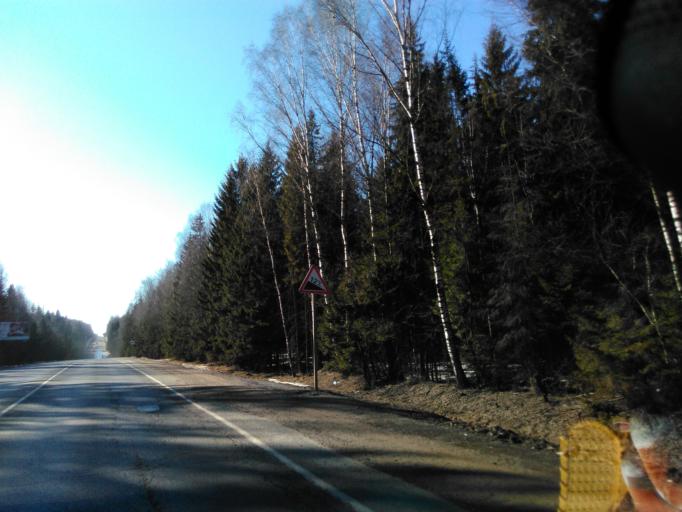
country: RU
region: Moskovskaya
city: Mendeleyevo
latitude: 56.1250
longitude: 37.3351
